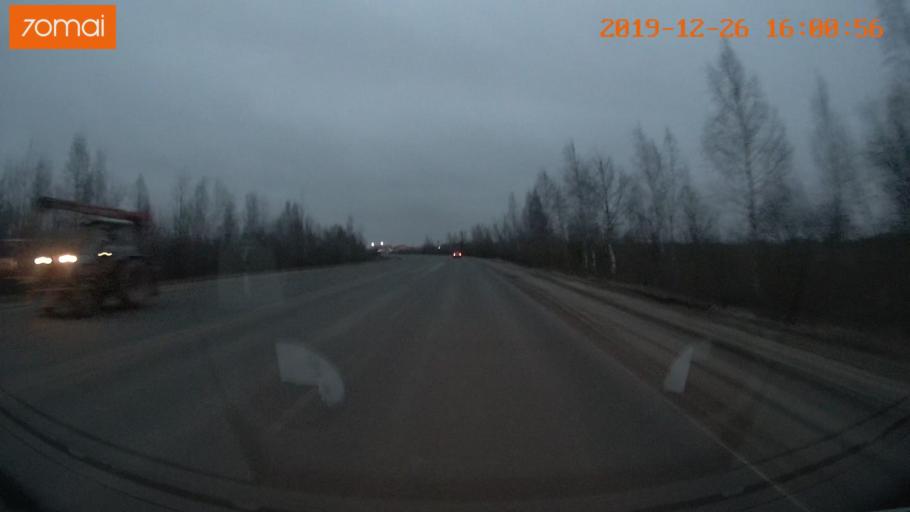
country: RU
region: Jaroslavl
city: Rybinsk
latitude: 58.0190
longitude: 38.8107
